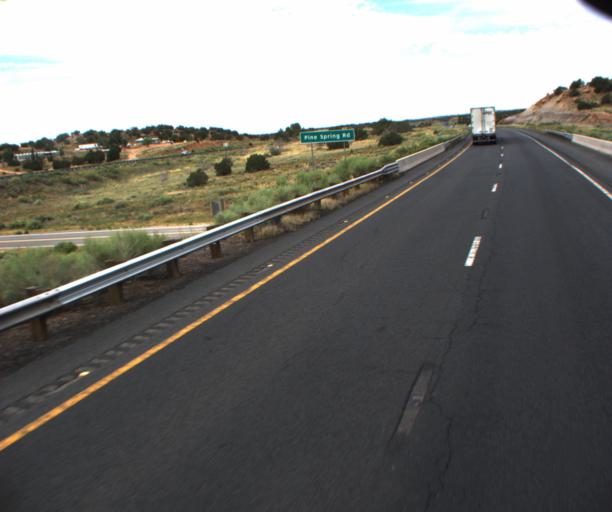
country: US
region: Arizona
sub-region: Apache County
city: Houck
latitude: 35.2825
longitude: -109.2396
